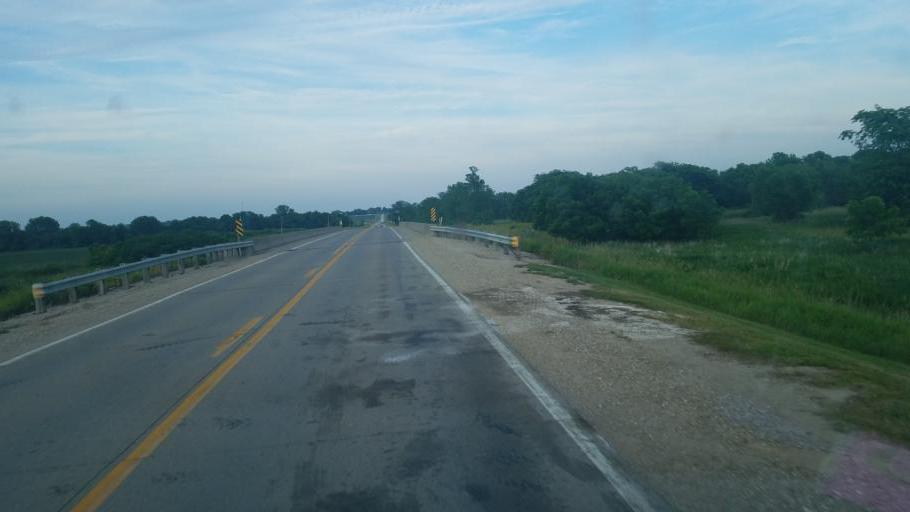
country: US
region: Iowa
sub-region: Benton County
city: Belle Plaine
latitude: 41.9062
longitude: -92.3072
